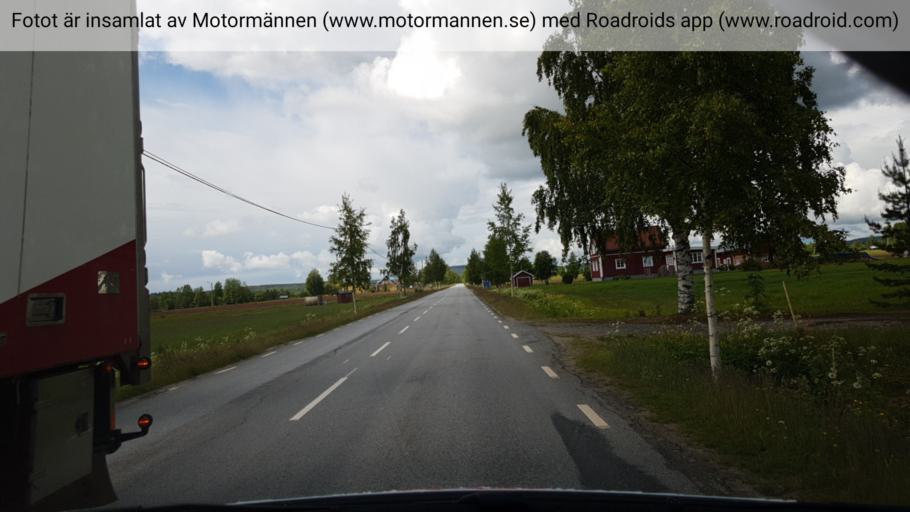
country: SE
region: Vaesterbotten
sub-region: Vannas Kommun
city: Vannasby
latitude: 63.9045
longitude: 19.8646
